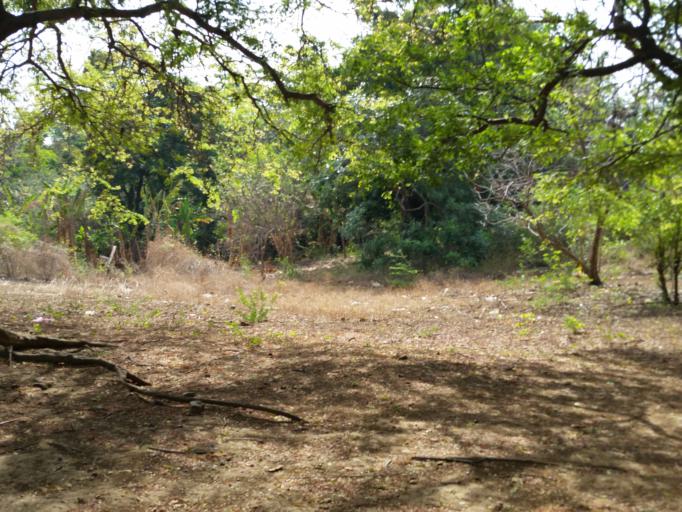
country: NI
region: Managua
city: Managua
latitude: 12.0804
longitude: -86.2544
